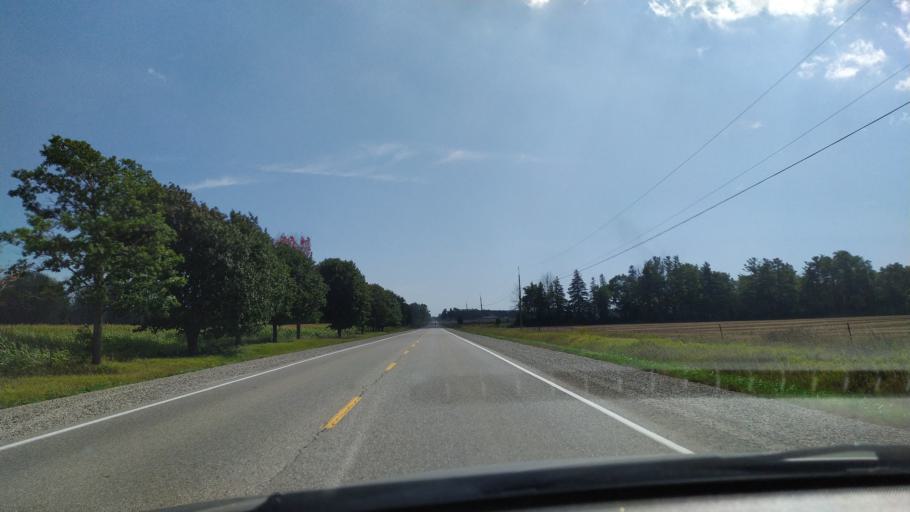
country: CA
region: Ontario
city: Ingersoll
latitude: 43.1147
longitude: -80.8809
